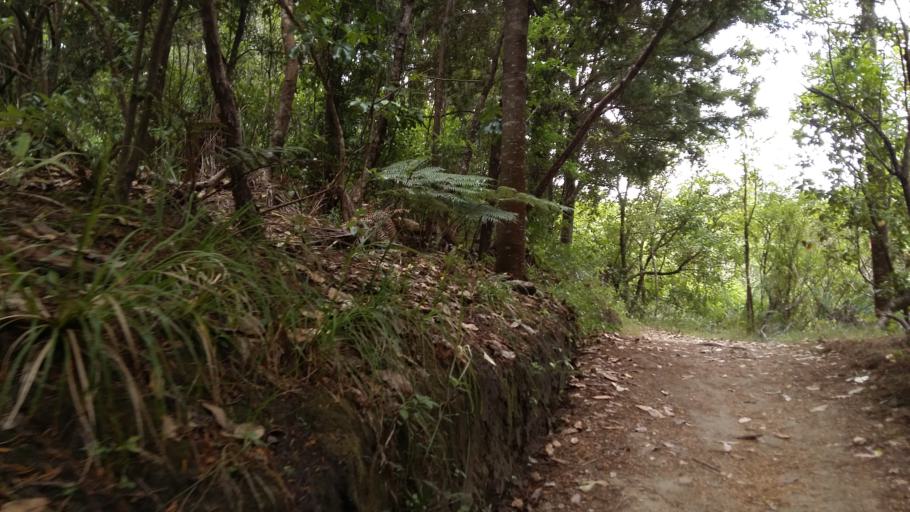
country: NZ
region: Bay of Plenty
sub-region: Whakatane District
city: Whakatane
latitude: -37.9533
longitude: 177.0038
